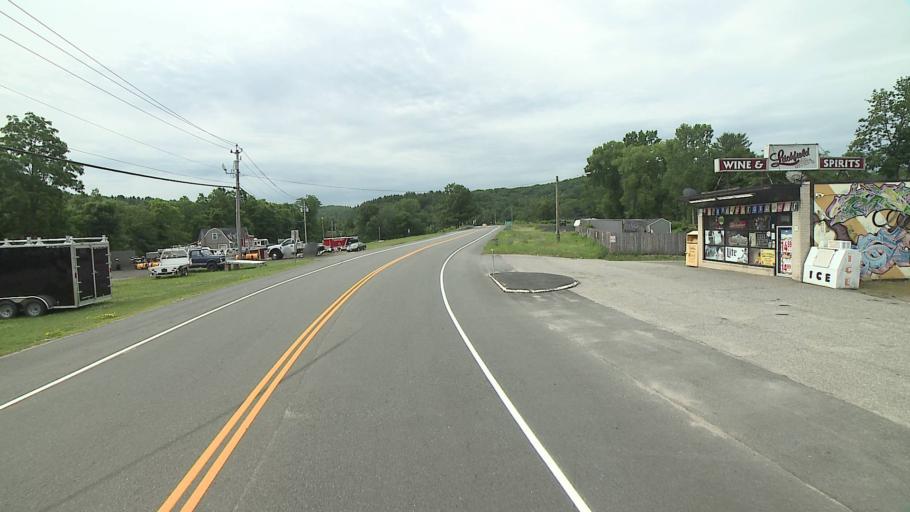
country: US
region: Connecticut
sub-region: Litchfield County
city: Torrington
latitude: 41.7666
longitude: -73.1170
